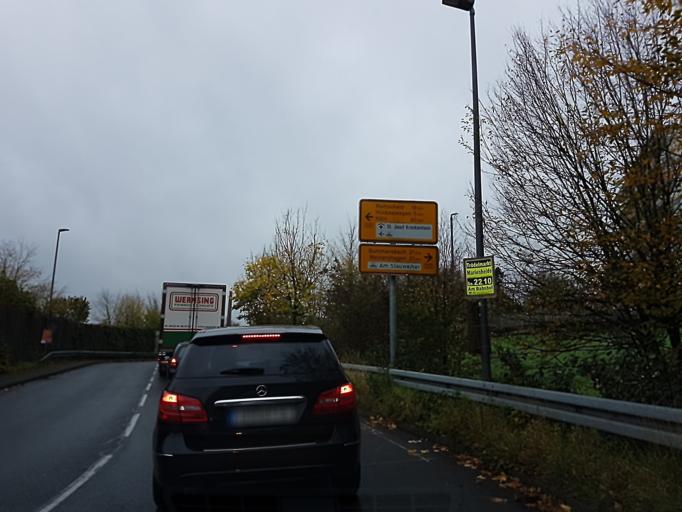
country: DE
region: North Rhine-Westphalia
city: Wipperfurth
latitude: 51.1207
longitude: 7.3993
